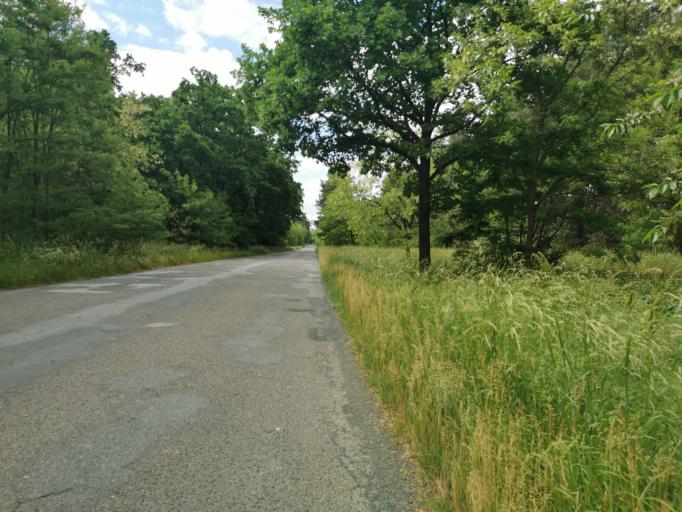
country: CZ
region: South Moravian
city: Rohatec
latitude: 48.8987
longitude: 17.1972
